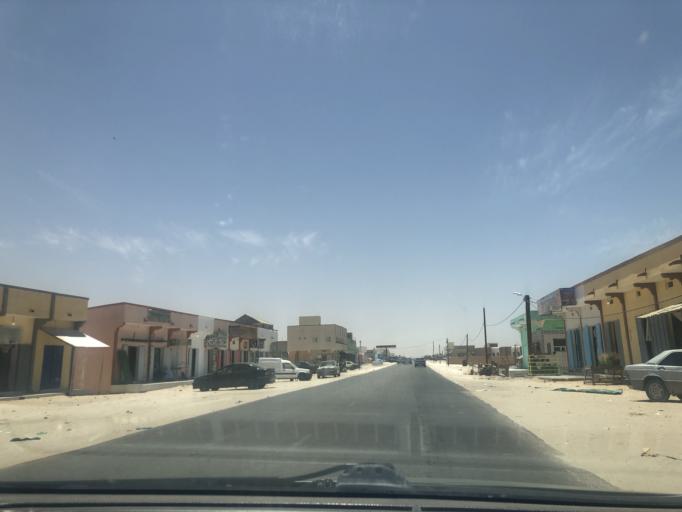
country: MR
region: Nouakchott
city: Nouakchott
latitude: 18.0168
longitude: -15.9589
